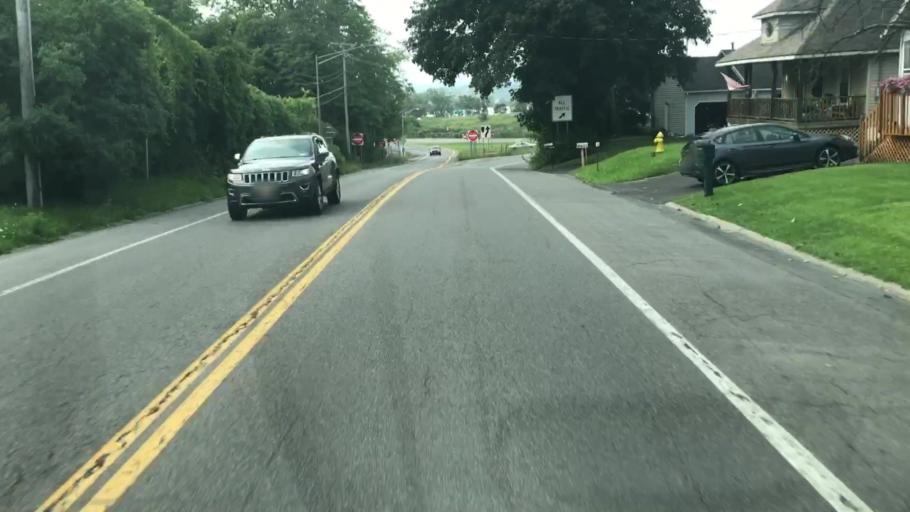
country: US
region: New York
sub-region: Onondaga County
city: Galeville
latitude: 43.0810
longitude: -76.1771
